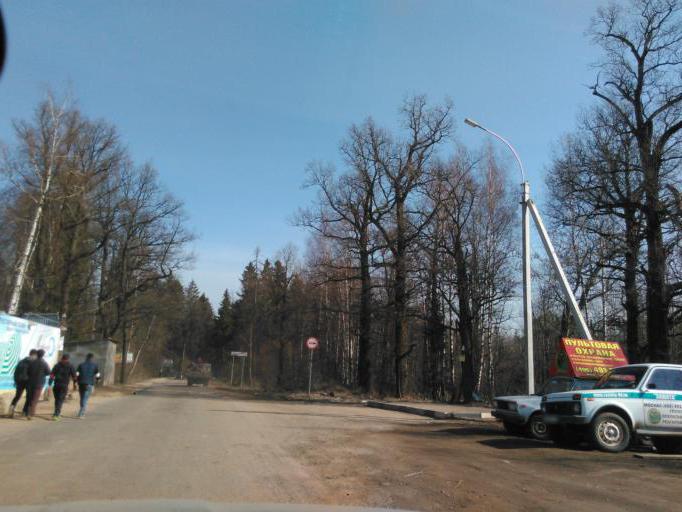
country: RU
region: Moskovskaya
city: Opalikha
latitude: 55.8875
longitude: 37.2655
